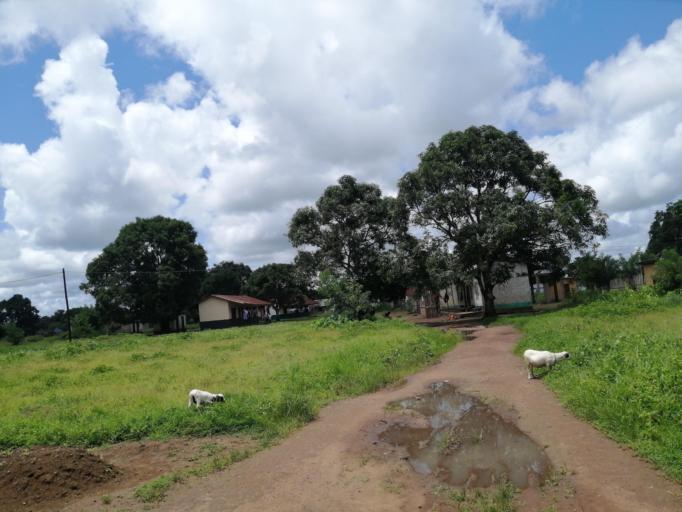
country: SL
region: Northern Province
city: Port Loko
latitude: 8.7761
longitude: -12.7892
